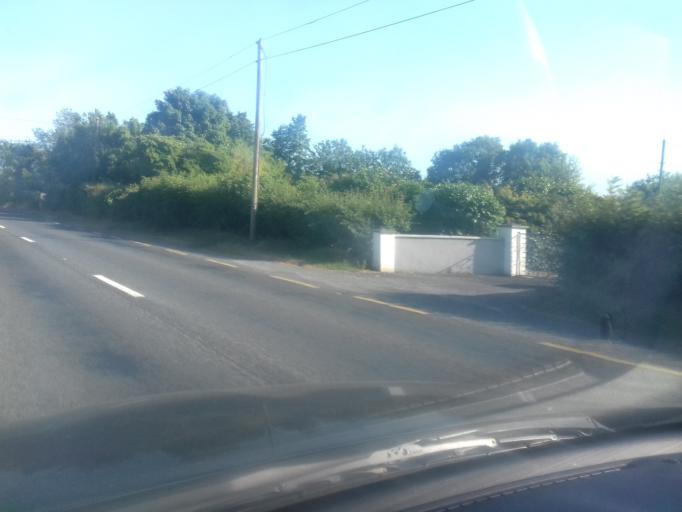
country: IE
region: Leinster
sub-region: An Mhi
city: Ashbourne
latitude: 53.4660
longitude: -6.3569
